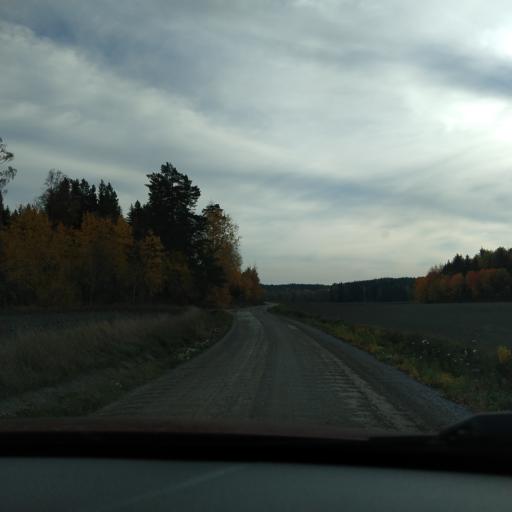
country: SE
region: Stockholm
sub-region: Vallentuna Kommun
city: Vallentuna
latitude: 59.5409
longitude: 18.0184
